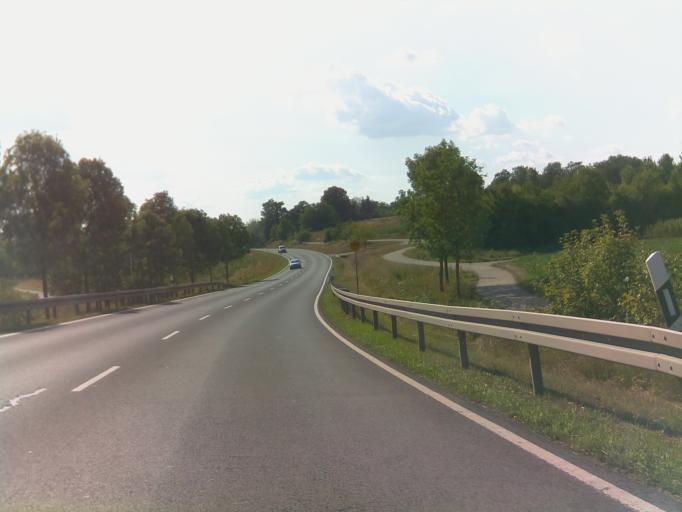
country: DE
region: Bavaria
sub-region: Regierungsbezirk Unterfranken
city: Grosseibstadt
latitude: 50.2992
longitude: 10.4387
